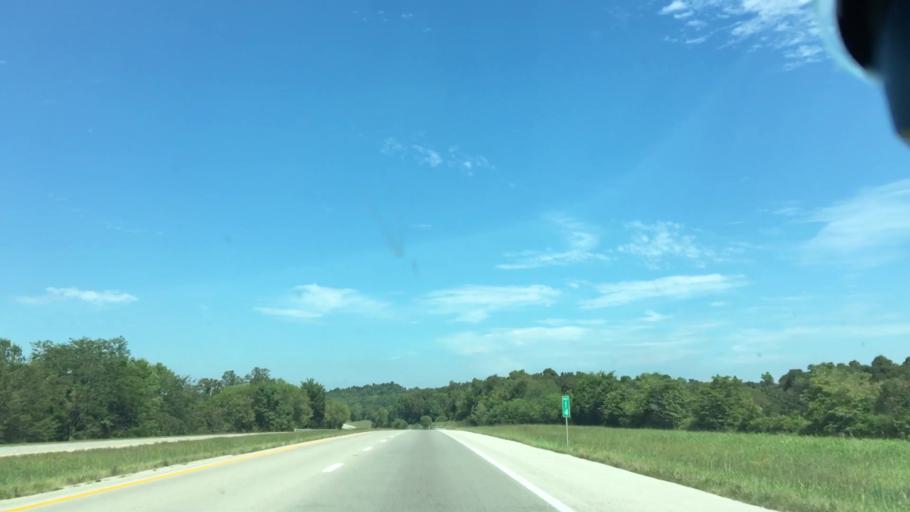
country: US
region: Kentucky
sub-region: Christian County
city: Hopkinsville
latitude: 36.9269
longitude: -87.4713
